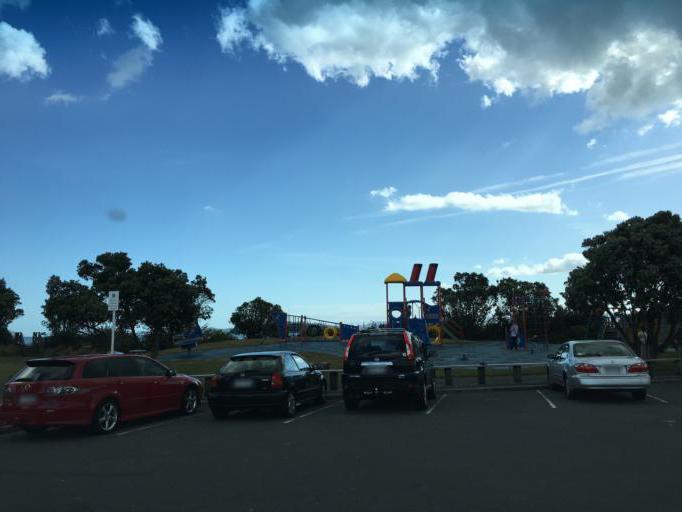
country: NZ
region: Wellington
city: Petone
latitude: -41.2320
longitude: 174.8902
